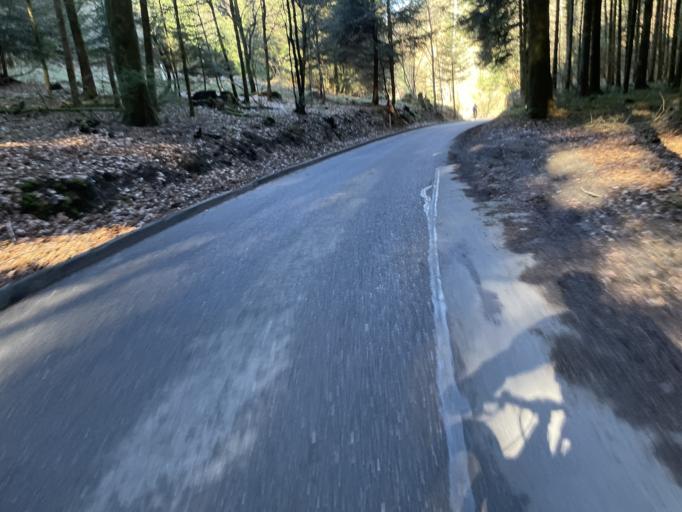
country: CH
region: Bern
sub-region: Bern-Mittelland District
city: Bariswil
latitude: 47.0046
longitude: 7.5362
